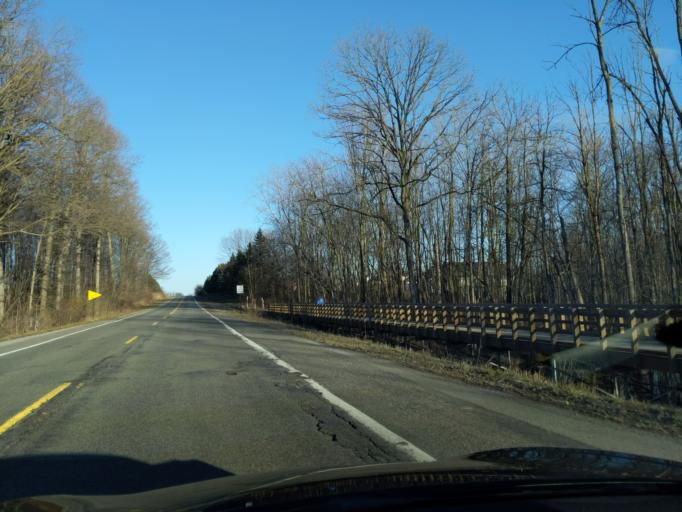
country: US
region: Michigan
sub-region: Ingham County
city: Mason
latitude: 42.5965
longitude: -84.4525
